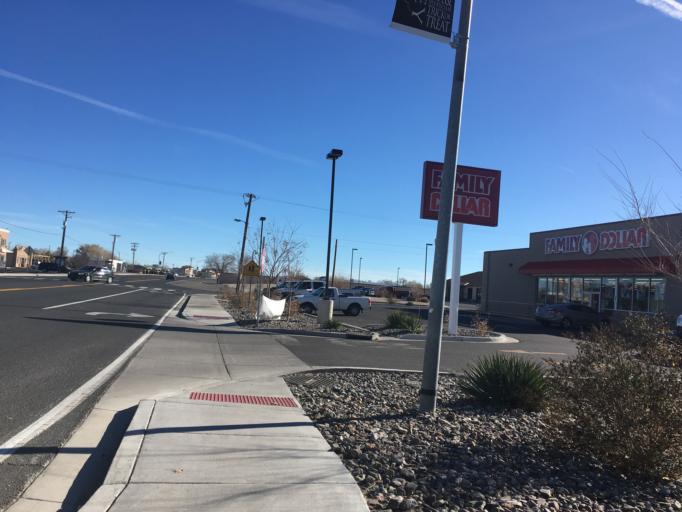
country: US
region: Nevada
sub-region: Lyon County
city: Fernley
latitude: 39.6076
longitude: -119.2472
